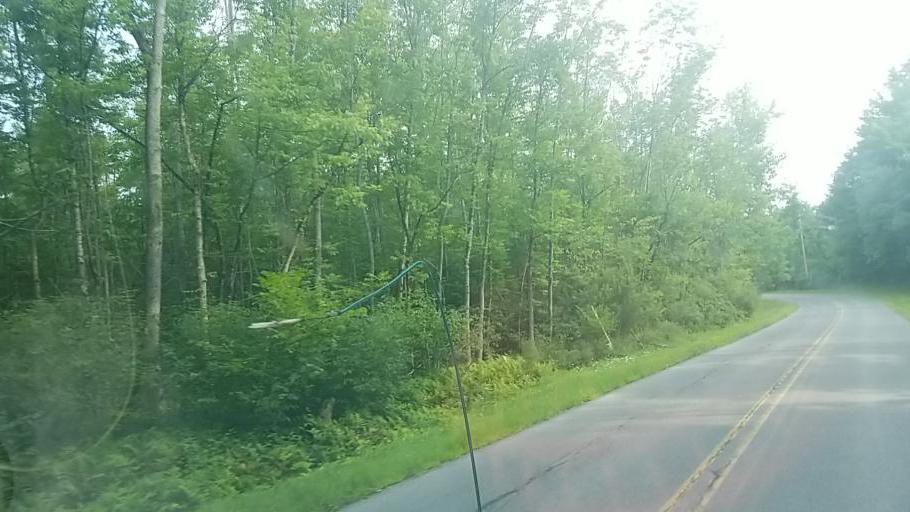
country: US
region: New York
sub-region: Fulton County
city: Broadalbin
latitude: 43.0767
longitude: -74.2234
